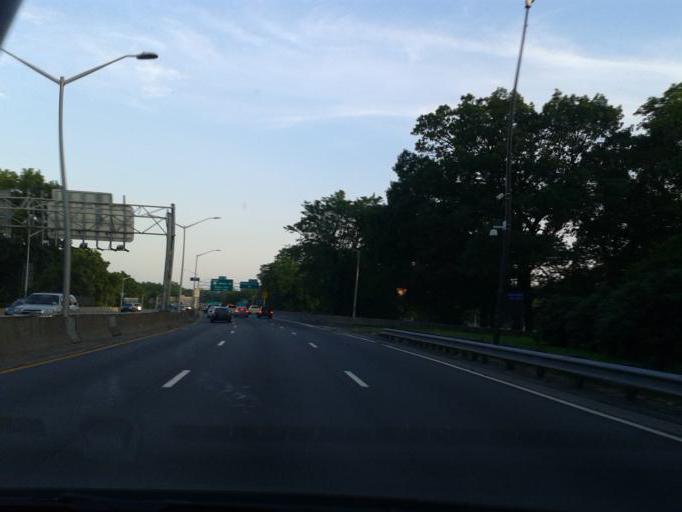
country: US
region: New York
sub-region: Bronx
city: The Bronx
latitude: 40.8573
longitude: -73.8727
